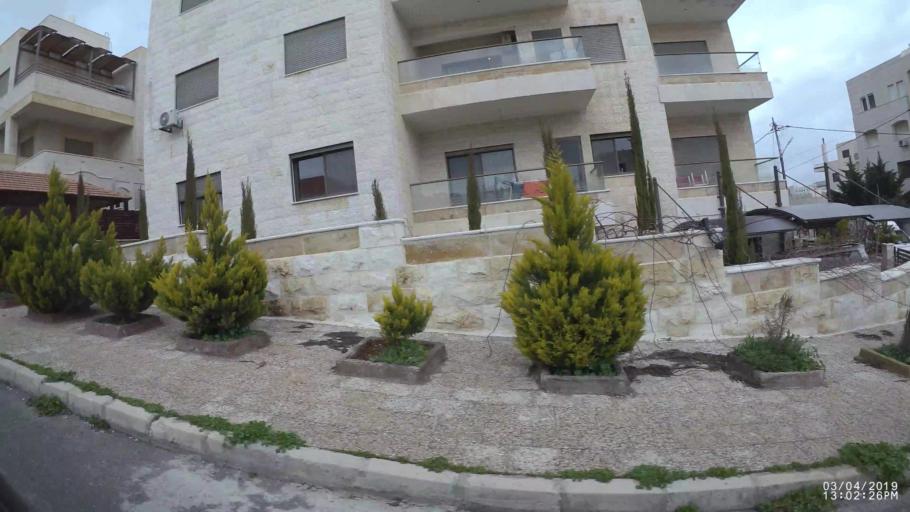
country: JO
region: Amman
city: Wadi as Sir
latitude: 31.9675
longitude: 35.8286
